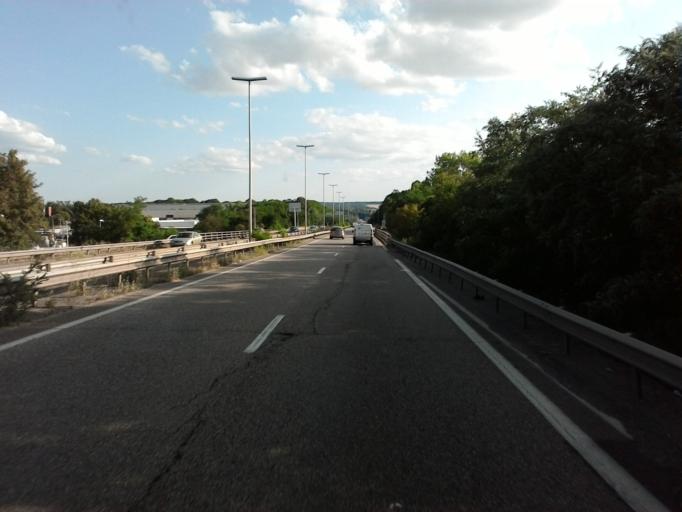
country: FR
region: Lorraine
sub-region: Departement de Meurthe-et-Moselle
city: Ludres
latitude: 48.6181
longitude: 6.1802
